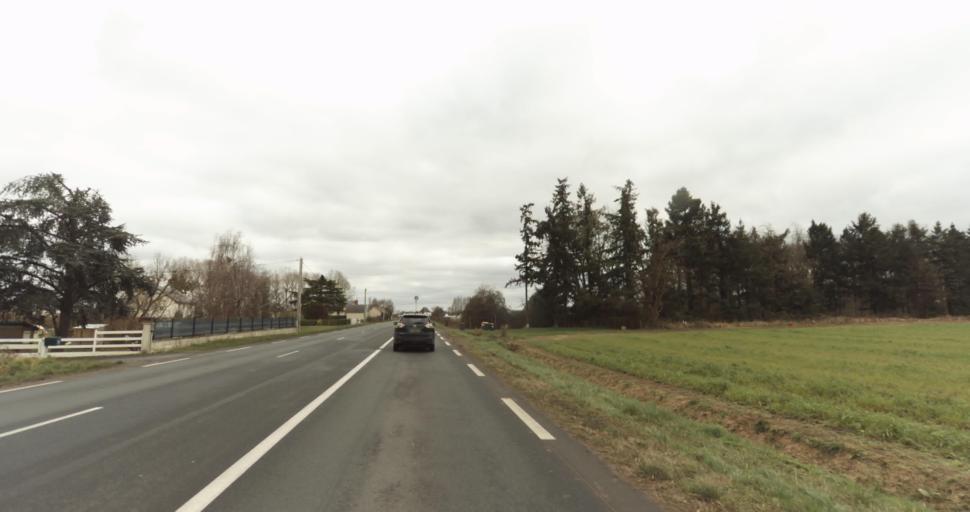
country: FR
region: Pays de la Loire
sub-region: Departement de Maine-et-Loire
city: Vivy
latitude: 47.3080
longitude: -0.0389
